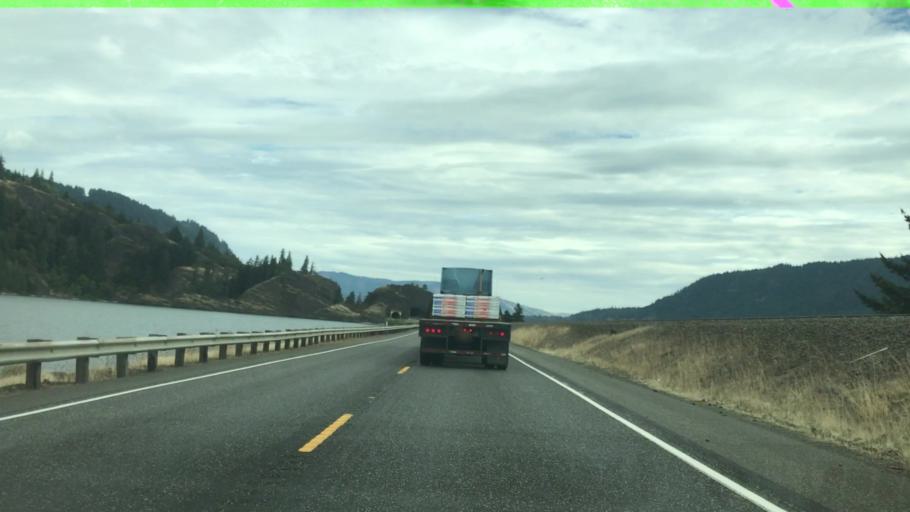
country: US
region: Oregon
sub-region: Hood River County
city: Hood River
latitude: 45.7100
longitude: -121.6343
